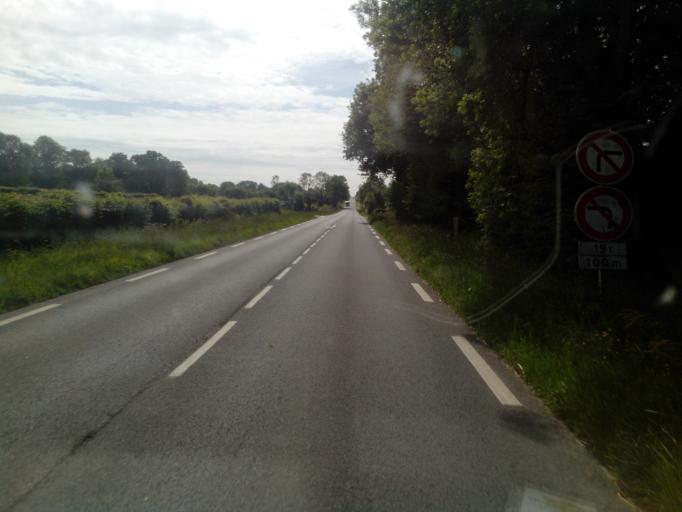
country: FR
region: Lower Normandy
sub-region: Departement du Calvados
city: Touques
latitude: 49.2575
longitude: 0.0797
